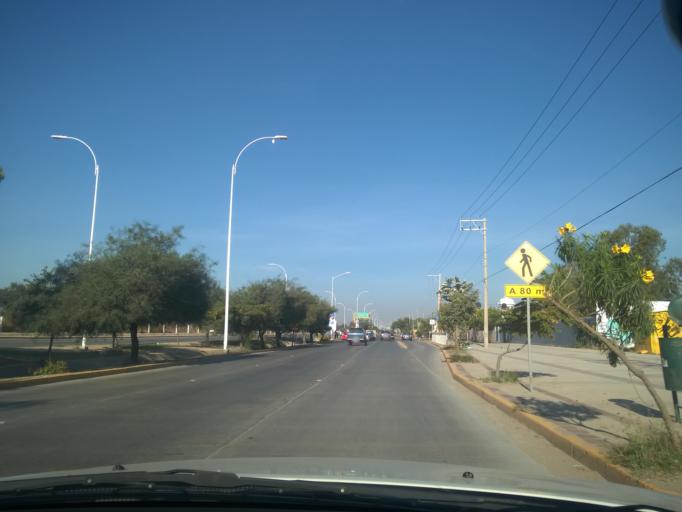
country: MX
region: Guanajuato
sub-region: Leon
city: San Jose de Duran (Los Troncoso)
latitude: 21.0722
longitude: -101.6446
